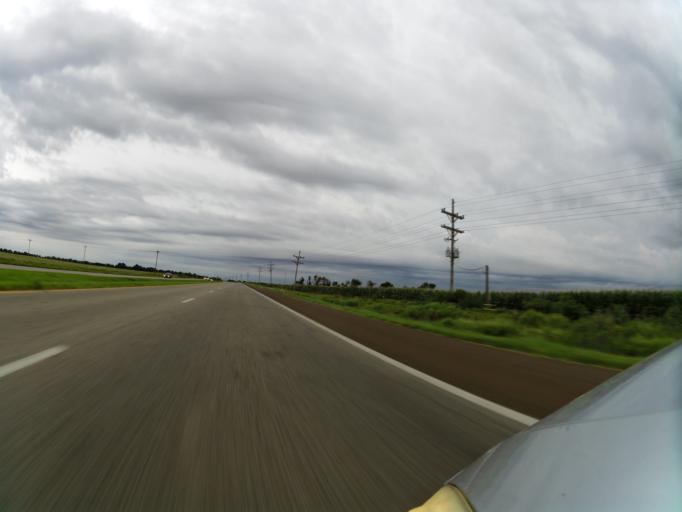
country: US
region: Kansas
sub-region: Reno County
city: South Hutchinson
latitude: 38.0015
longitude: -97.9407
